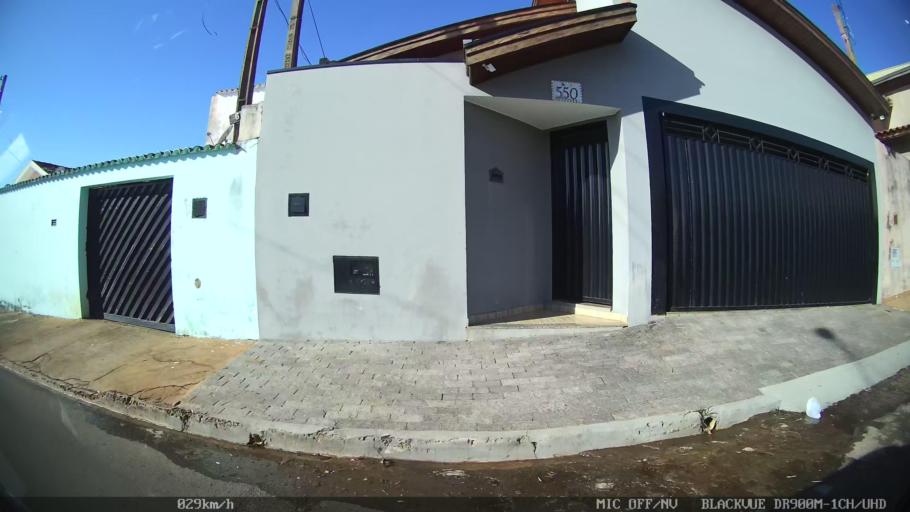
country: BR
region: Sao Paulo
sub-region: Franca
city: Franca
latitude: -20.5135
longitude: -47.4117
